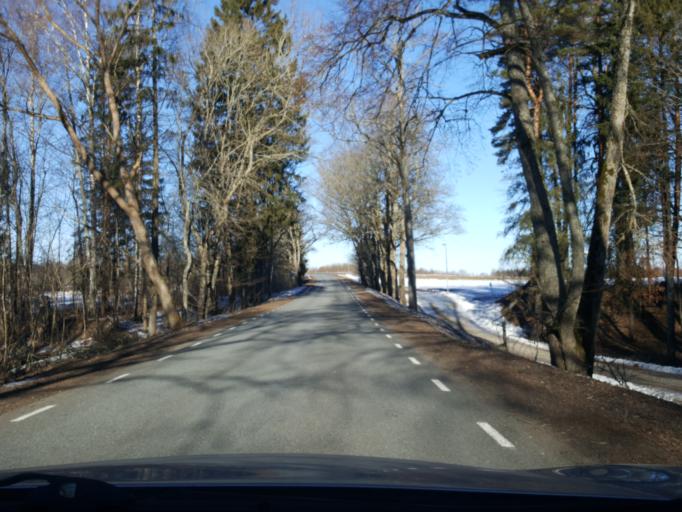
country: EE
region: Viljandimaa
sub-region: Vohma linn
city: Vohma
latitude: 58.5595
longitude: 25.5540
